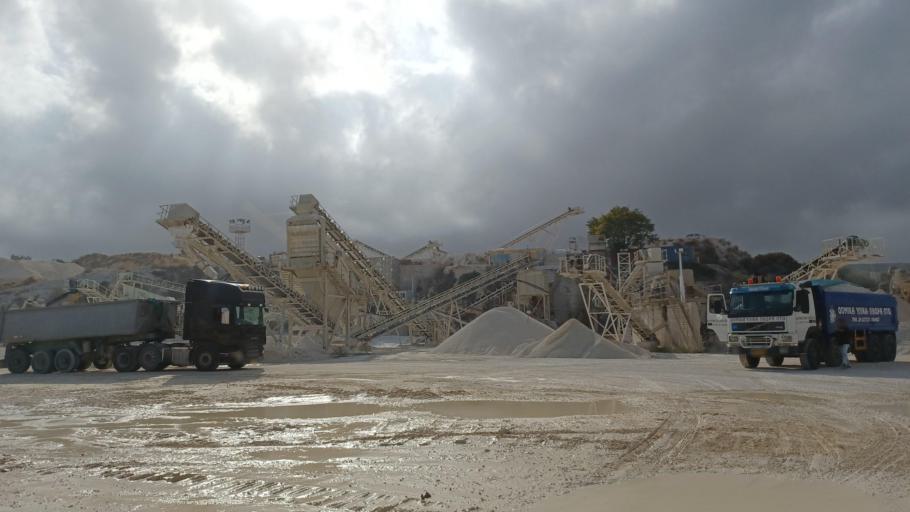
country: CY
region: Pafos
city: Polis
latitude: 35.0003
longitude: 32.3942
